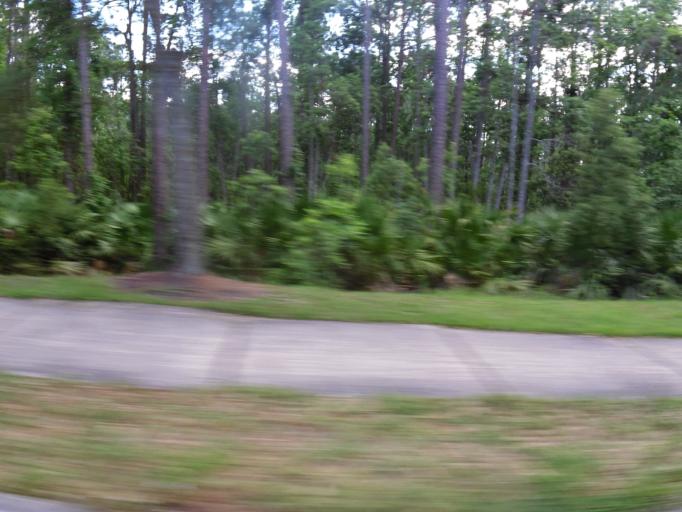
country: US
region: Florida
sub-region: Duval County
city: Jacksonville
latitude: 30.2446
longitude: -81.5937
